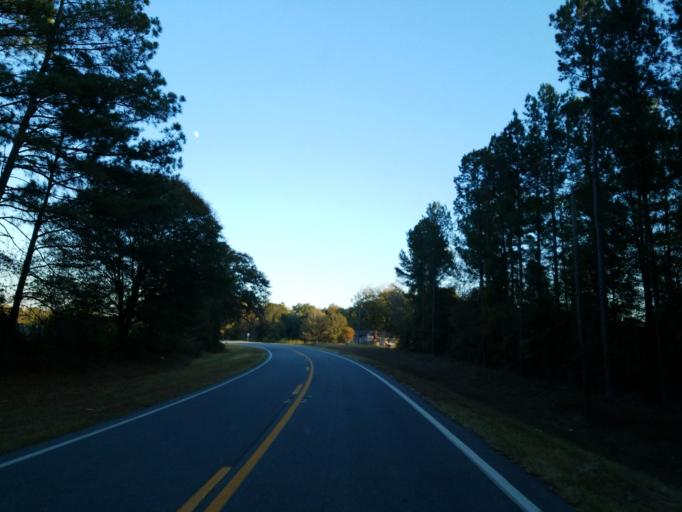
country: US
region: Georgia
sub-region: Wilcox County
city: Rochelle
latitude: 31.8111
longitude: -83.4967
